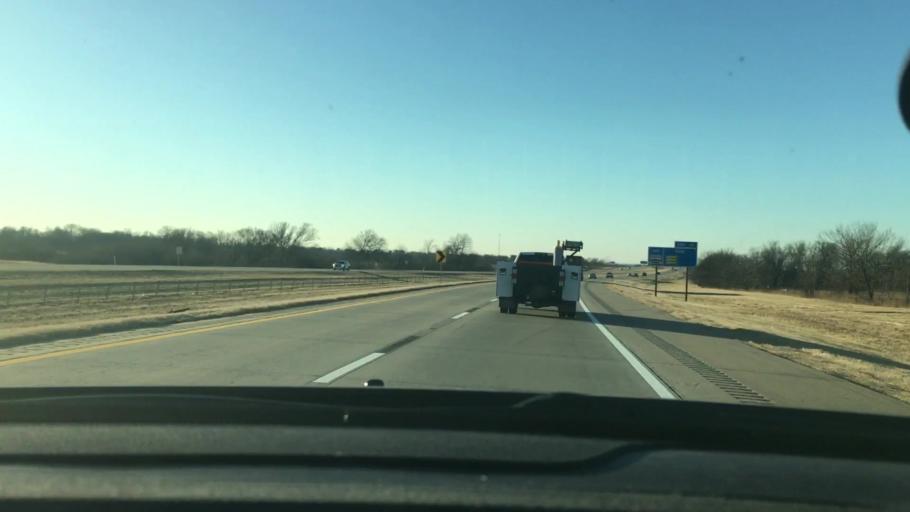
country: US
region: Oklahoma
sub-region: Murray County
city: Davis
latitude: 34.3441
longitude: -97.1483
